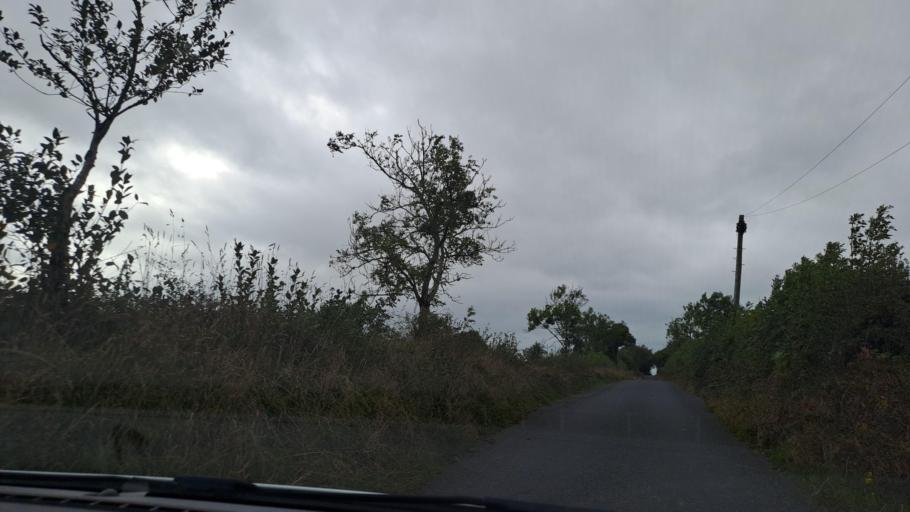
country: IE
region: Ulster
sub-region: An Cabhan
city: Bailieborough
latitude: 54.0141
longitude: -6.8807
